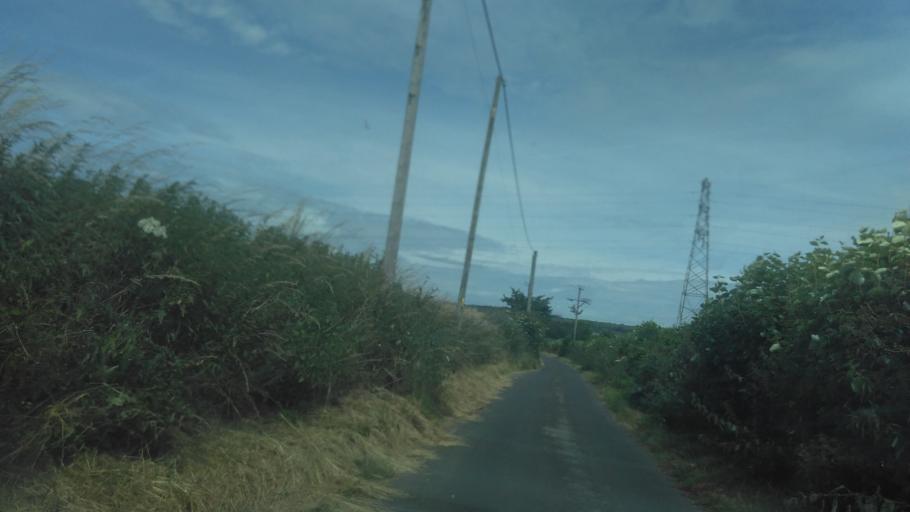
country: GB
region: England
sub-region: Kent
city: Chartham
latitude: 51.2493
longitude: 1.0024
